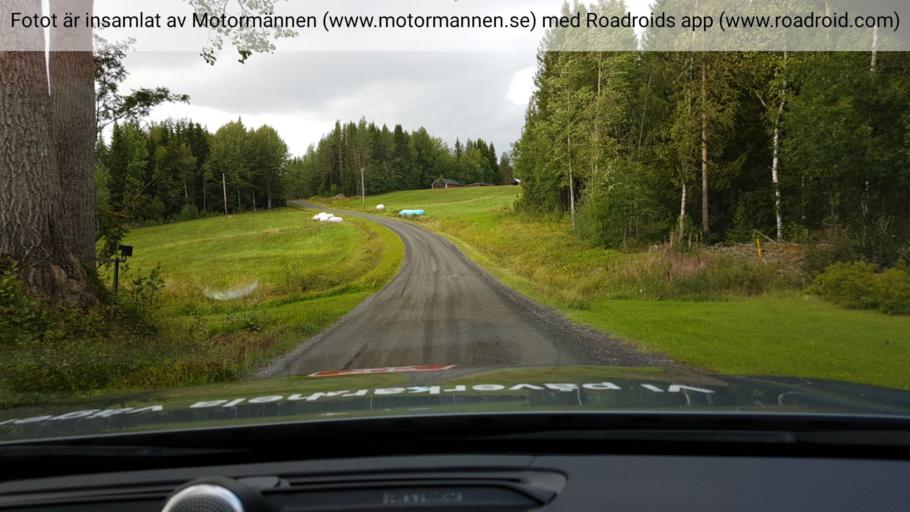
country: SE
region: Jaemtland
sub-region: OEstersunds Kommun
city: Lit
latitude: 63.7736
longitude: 14.6535
